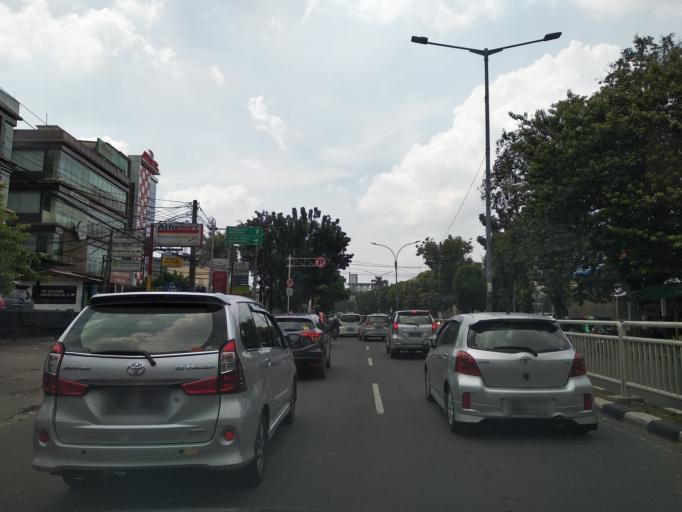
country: ID
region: Jakarta Raya
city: Jakarta
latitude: -6.2298
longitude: 106.8471
